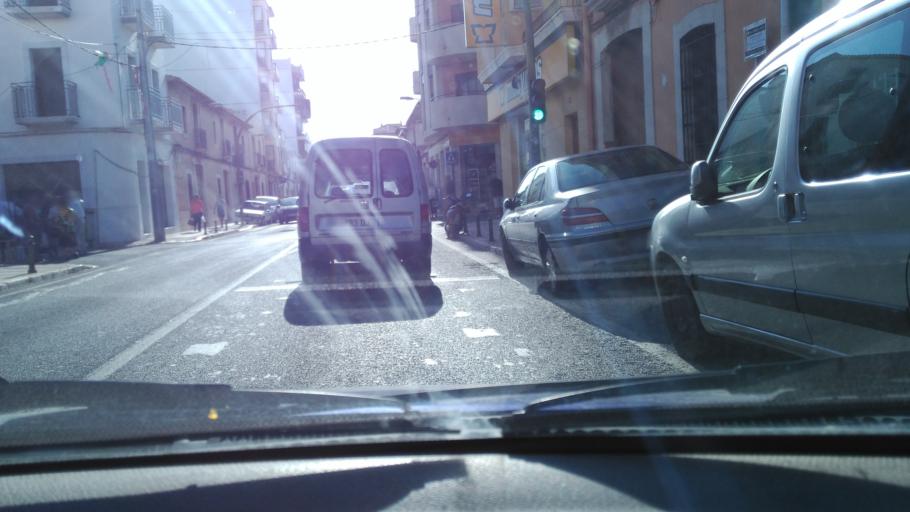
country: ES
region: Valencia
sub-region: Provincia de Alicante
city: Gata de Gorgos
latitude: 38.7745
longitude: 0.0858
